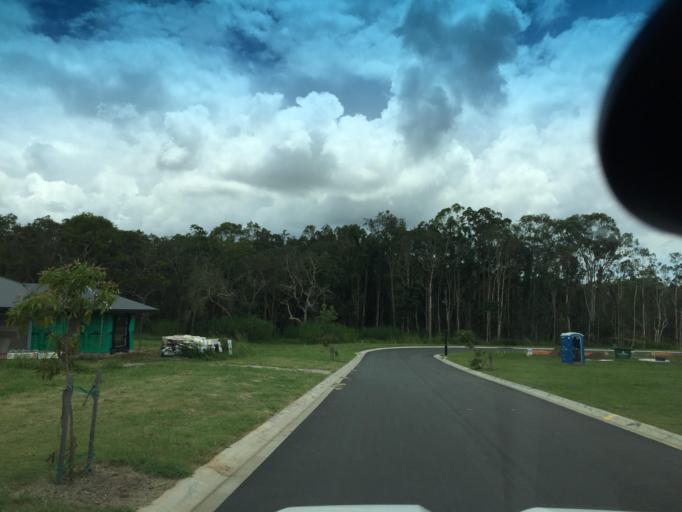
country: AU
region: Queensland
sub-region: Moreton Bay
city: Caboolture
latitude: -27.0410
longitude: 152.9202
